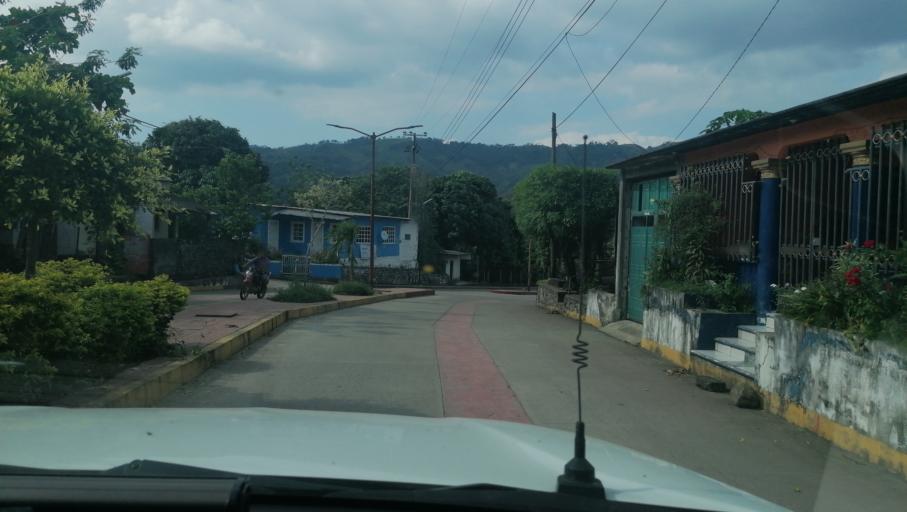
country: MX
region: Chiapas
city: Ostuacan
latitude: 17.4097
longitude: -93.3360
